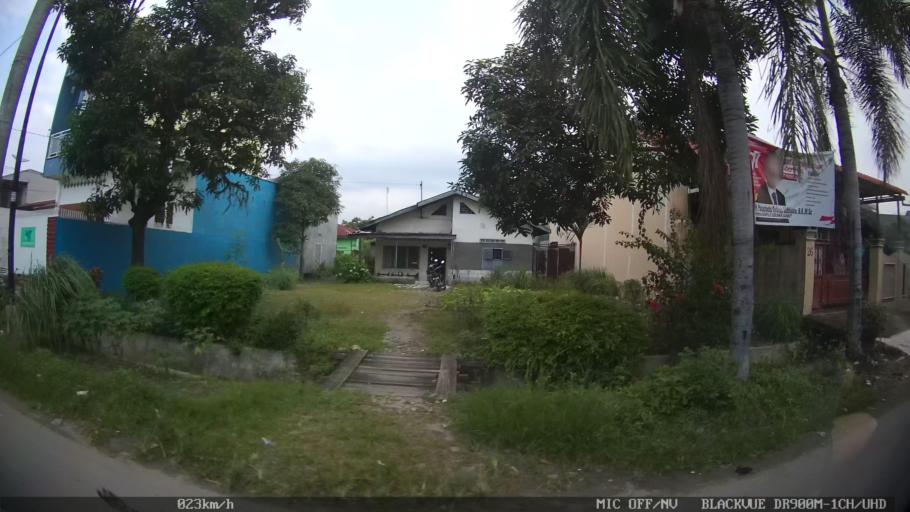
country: ID
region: North Sumatra
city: Medan
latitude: 3.6098
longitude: 98.6866
